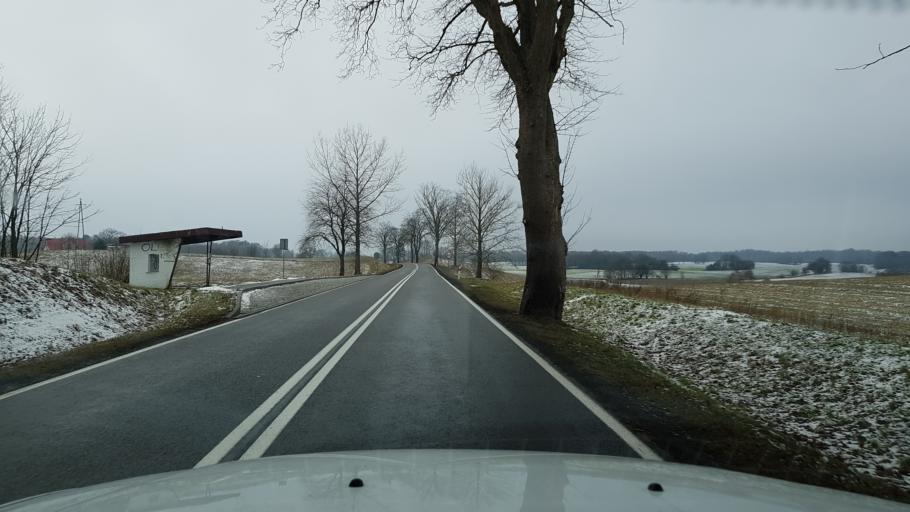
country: PL
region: West Pomeranian Voivodeship
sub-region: Powiat drawski
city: Czaplinek
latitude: 53.5602
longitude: 16.1967
